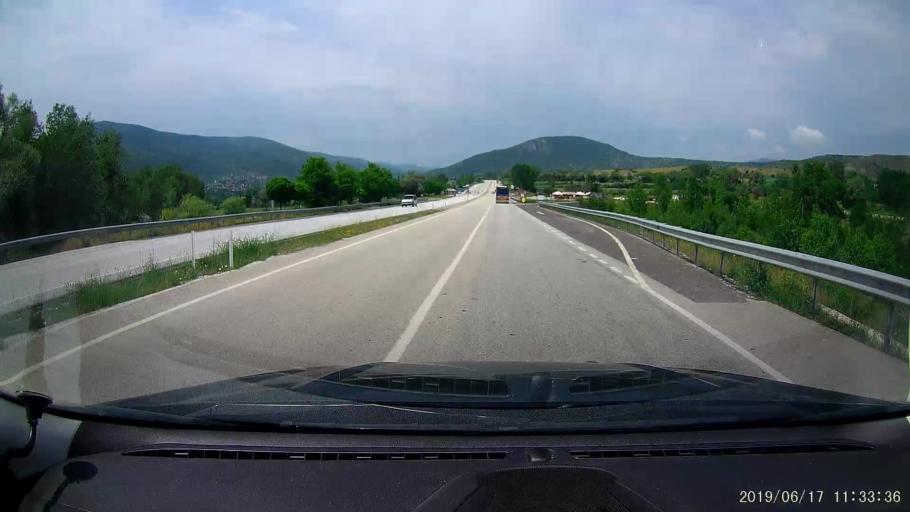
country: TR
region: Cankiri
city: Beloren
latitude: 40.8776
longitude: 33.5108
